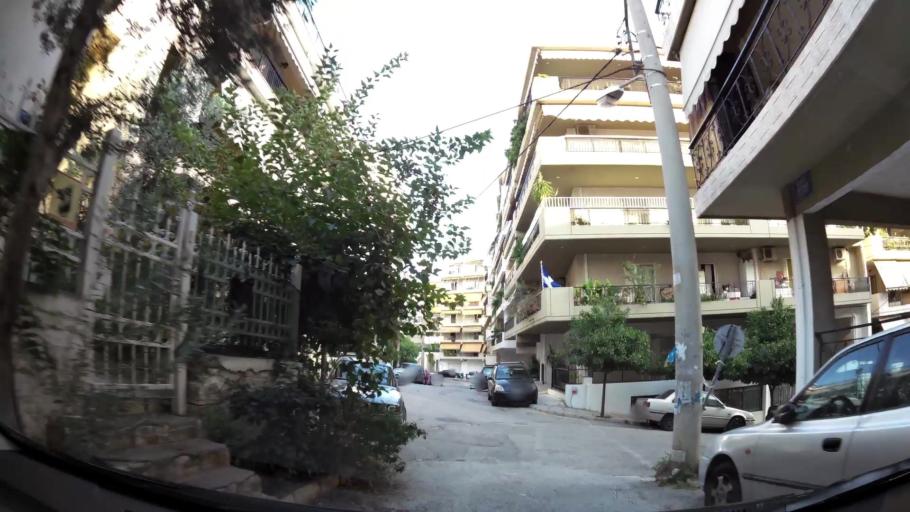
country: GR
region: Attica
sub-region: Nomarchia Athinas
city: Nea Ionia
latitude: 38.0286
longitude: 23.7500
